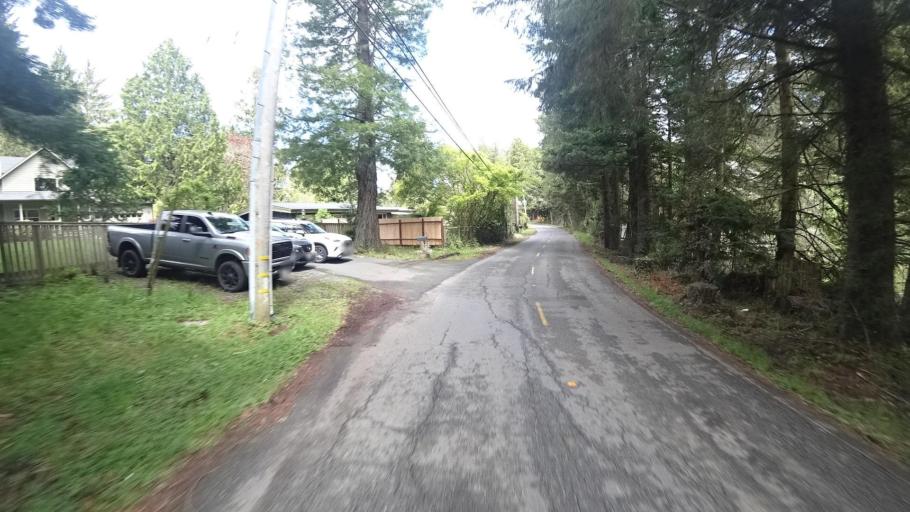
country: US
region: California
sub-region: Humboldt County
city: Bayside
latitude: 40.8636
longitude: -124.0427
